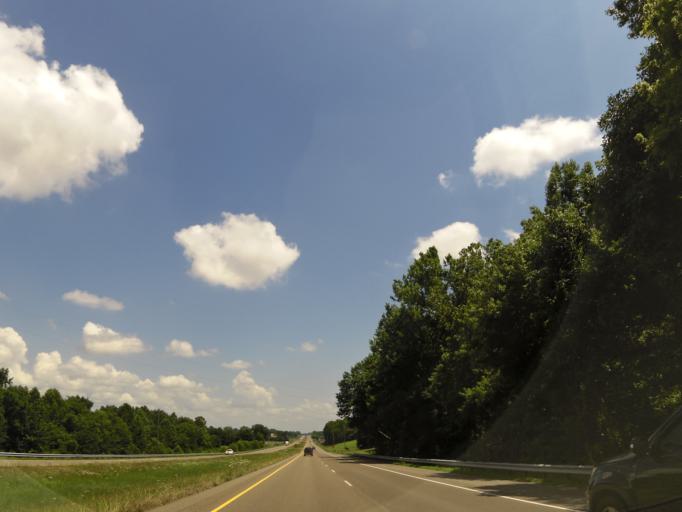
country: US
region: Tennessee
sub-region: Lauderdale County
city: Halls
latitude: 35.9067
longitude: -89.2578
